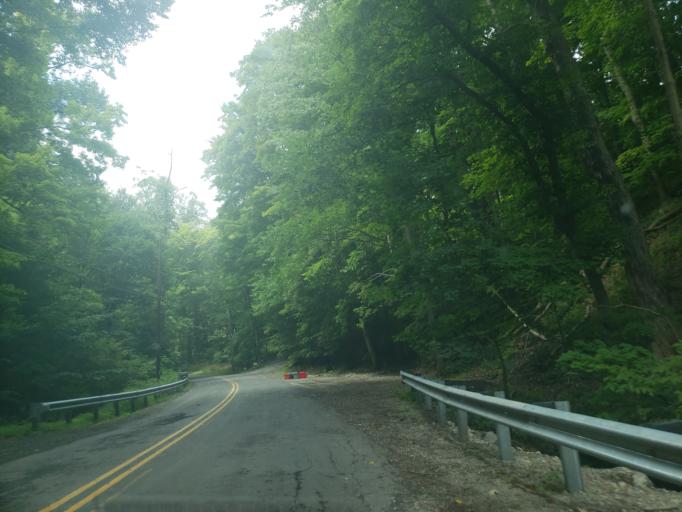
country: US
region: Pennsylvania
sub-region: Allegheny County
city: Coraopolis
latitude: 40.5371
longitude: -80.1321
